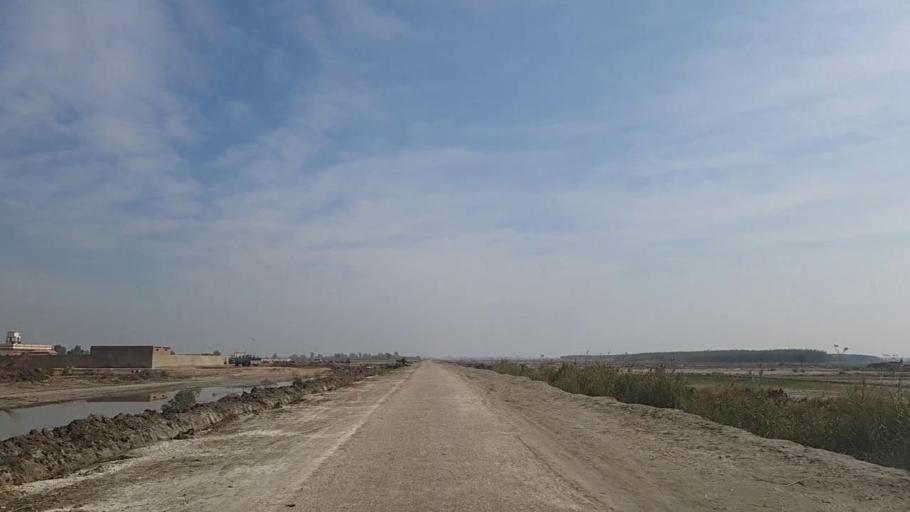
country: PK
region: Sindh
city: Nawabshah
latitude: 26.3319
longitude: 68.4534
